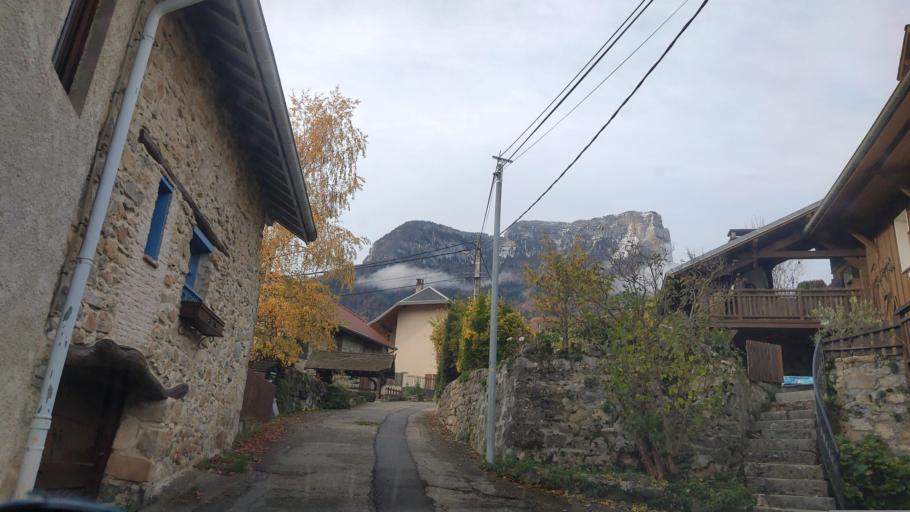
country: FR
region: Rhone-Alpes
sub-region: Departement de l'Isere
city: Chapareillan
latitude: 45.4794
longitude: 5.9709
